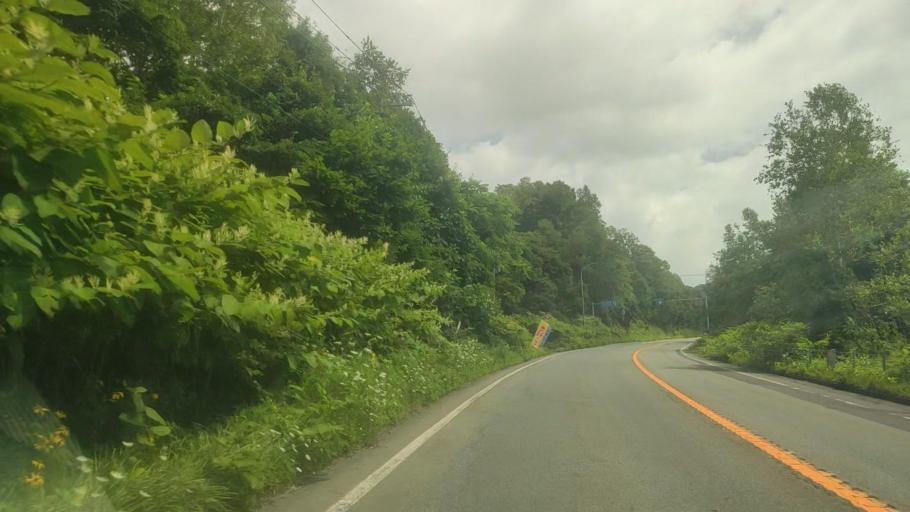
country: JP
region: Hokkaido
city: Niseko Town
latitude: 42.6004
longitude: 140.6624
